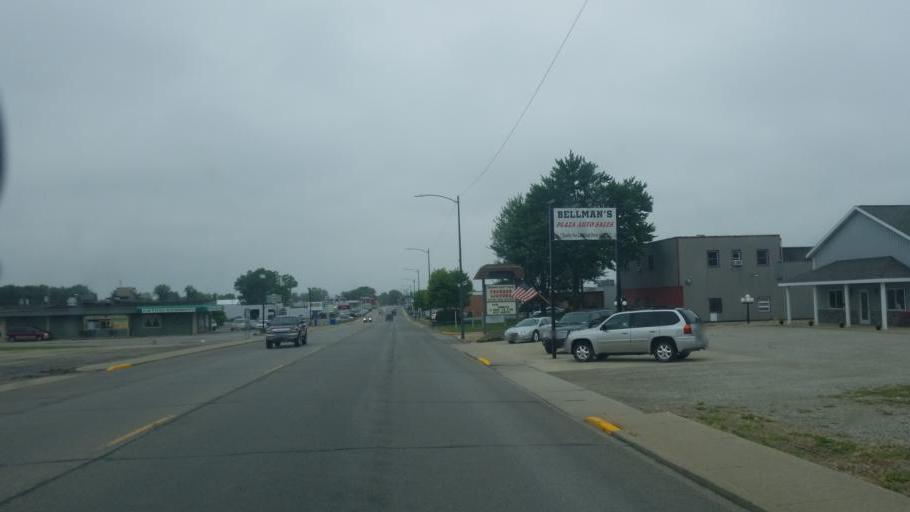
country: US
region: Indiana
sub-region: Marshall County
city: Bremen
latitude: 41.4465
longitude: -86.1578
